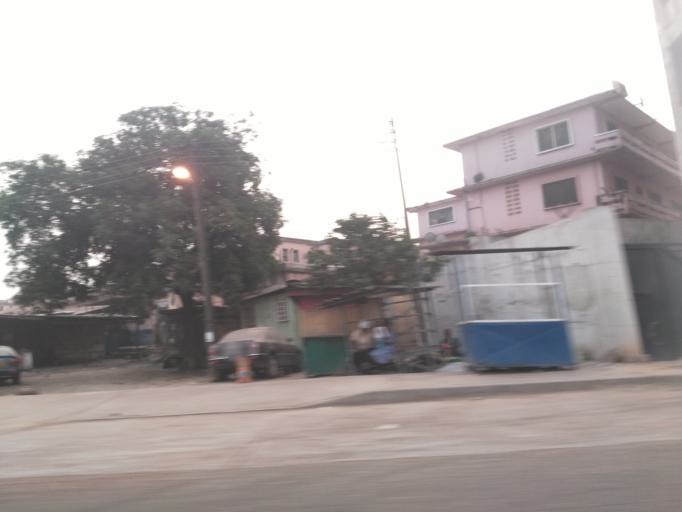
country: GH
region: Ashanti
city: Kumasi
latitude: 6.6829
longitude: -1.6109
